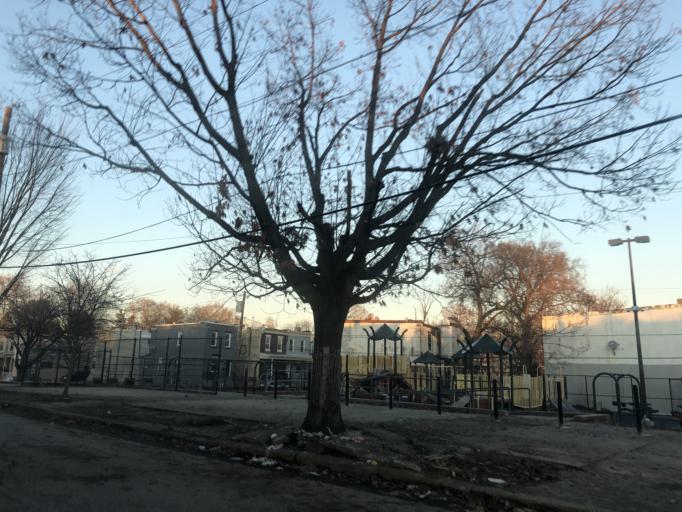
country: US
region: Pennsylvania
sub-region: Delaware County
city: Millbourne
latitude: 39.9669
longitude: -75.2230
